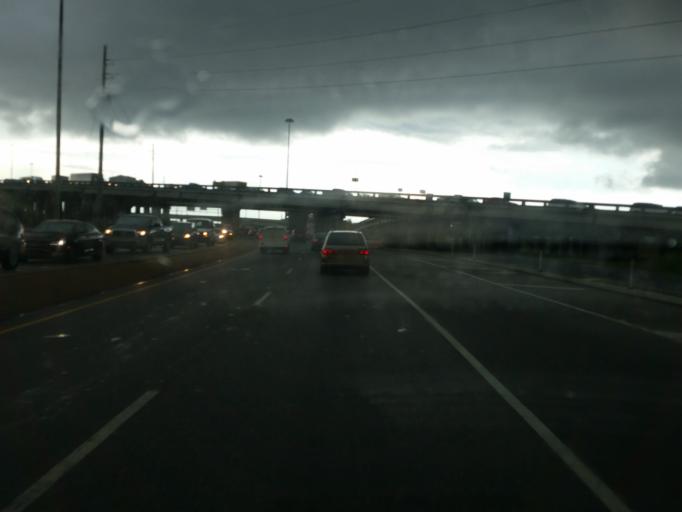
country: US
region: Alabama
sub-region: Mobile County
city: Mobile
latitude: 30.6927
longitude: -88.0293
